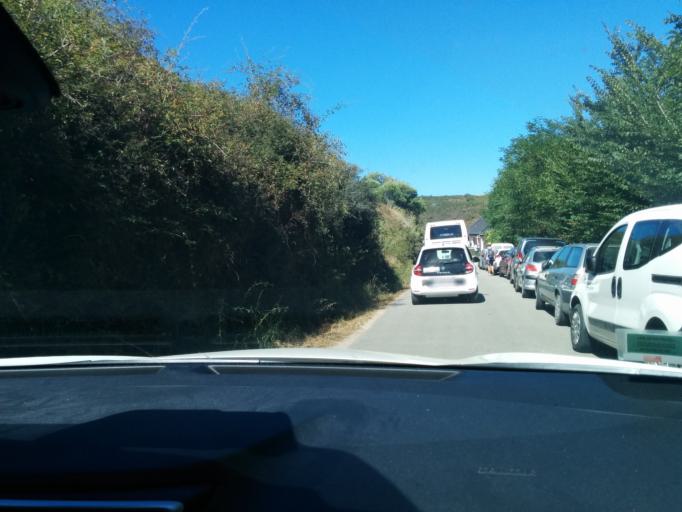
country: FR
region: Brittany
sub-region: Departement du Morbihan
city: Le Palais
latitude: 47.3064
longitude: -3.0655
